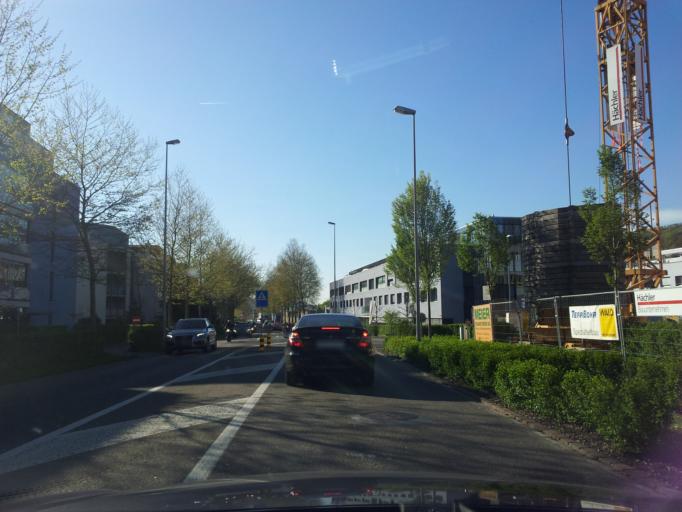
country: CH
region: Aargau
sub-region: Bezirk Baden
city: Neuenhof
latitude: 47.4599
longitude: 8.3406
